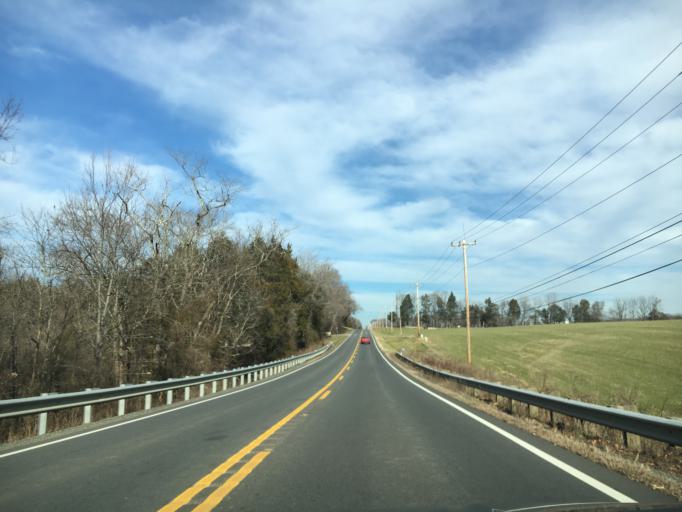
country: US
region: Virginia
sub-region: Fauquier County
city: Warrenton
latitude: 38.6371
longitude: -77.9332
